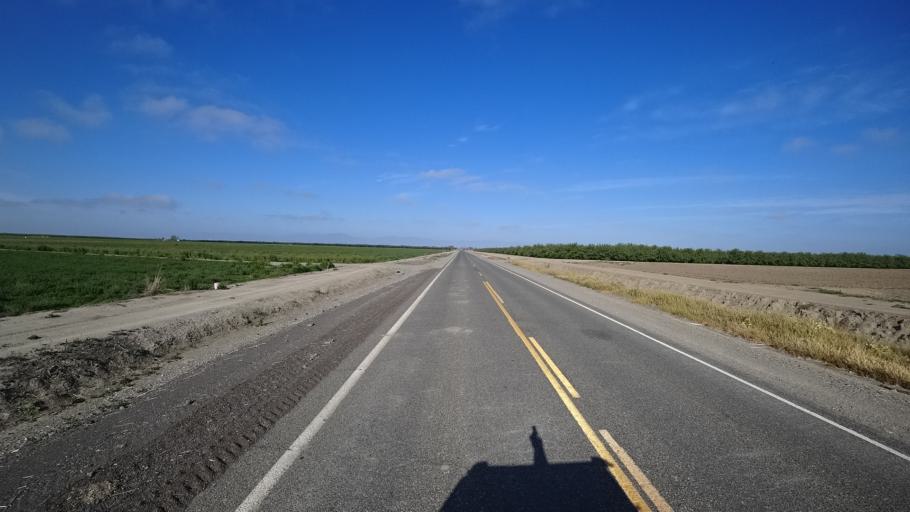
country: US
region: California
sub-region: Glenn County
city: Willows
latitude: 39.5822
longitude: -122.1274
